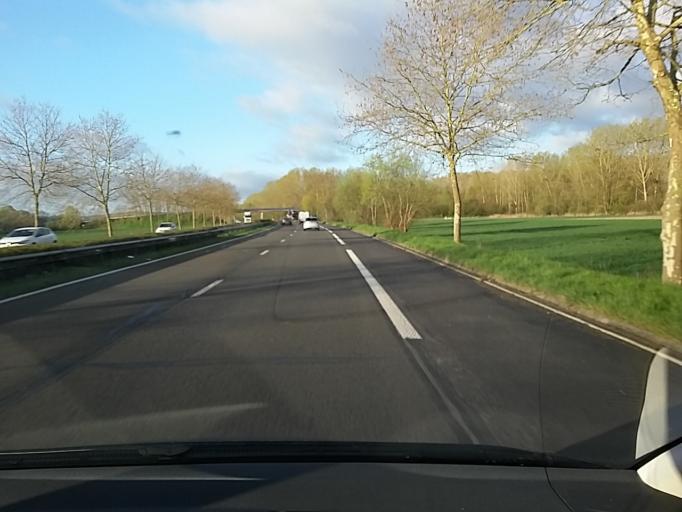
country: FR
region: Picardie
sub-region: Departement de l'Oise
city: Le Meux
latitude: 49.3474
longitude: 2.7422
